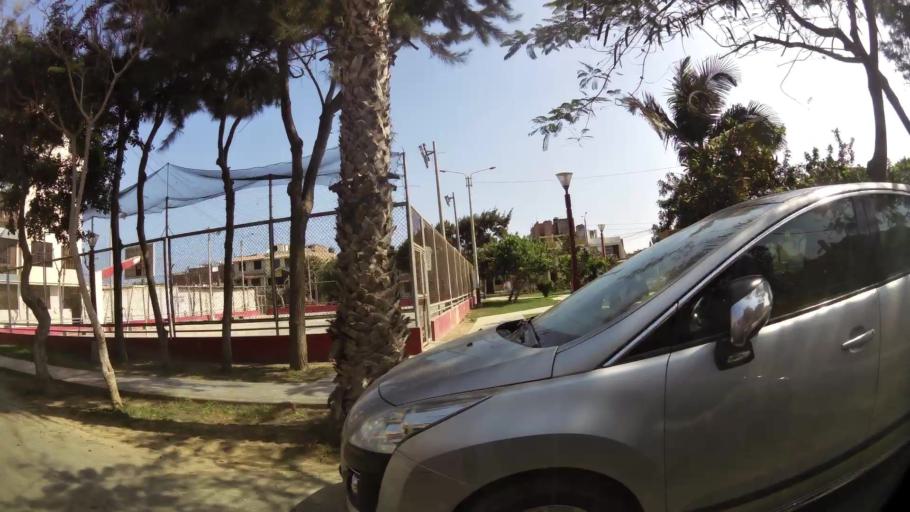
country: PE
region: La Libertad
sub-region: Provincia de Trujillo
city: Buenos Aires
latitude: -8.1320
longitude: -79.0464
